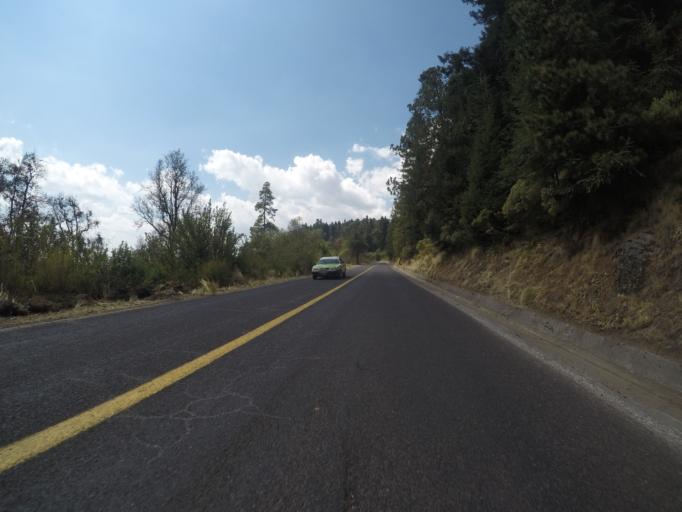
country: MX
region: Mexico
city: Cerro La Calera
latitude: 19.1437
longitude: -99.8050
